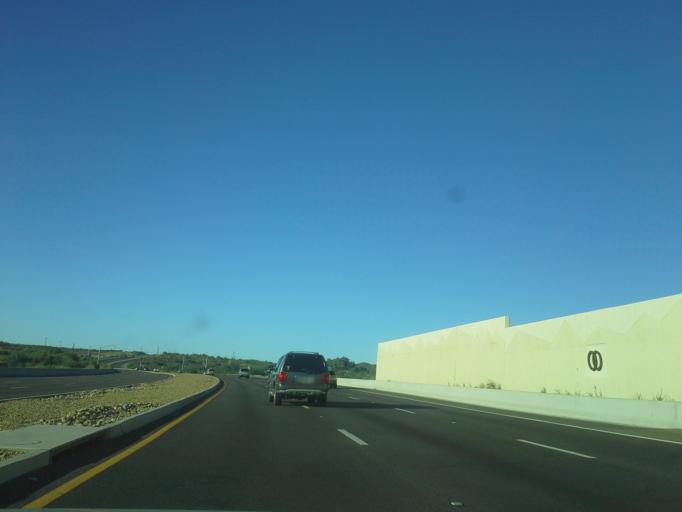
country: US
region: Arizona
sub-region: Pima County
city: Oro Valley
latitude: 32.4134
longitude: -110.9385
